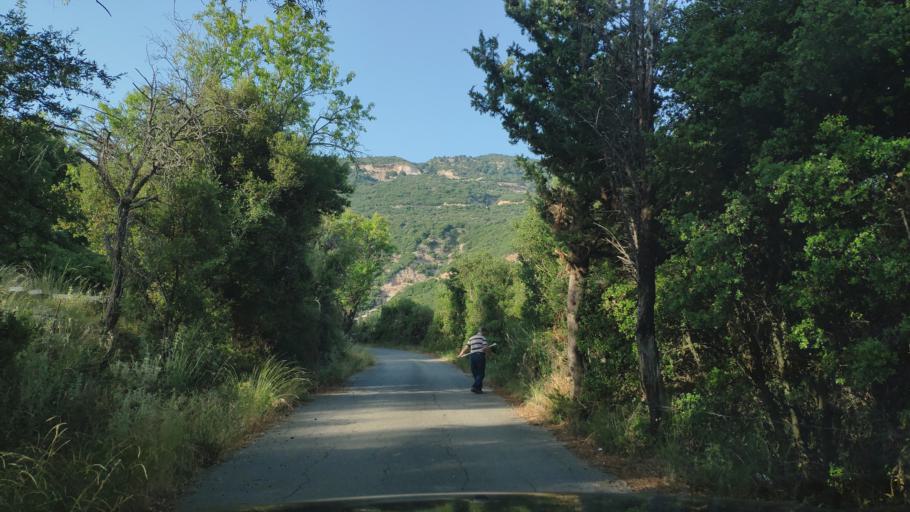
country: GR
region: West Greece
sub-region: Nomos Aitolias kai Akarnanias
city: Monastirakion
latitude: 38.8507
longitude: 20.9795
